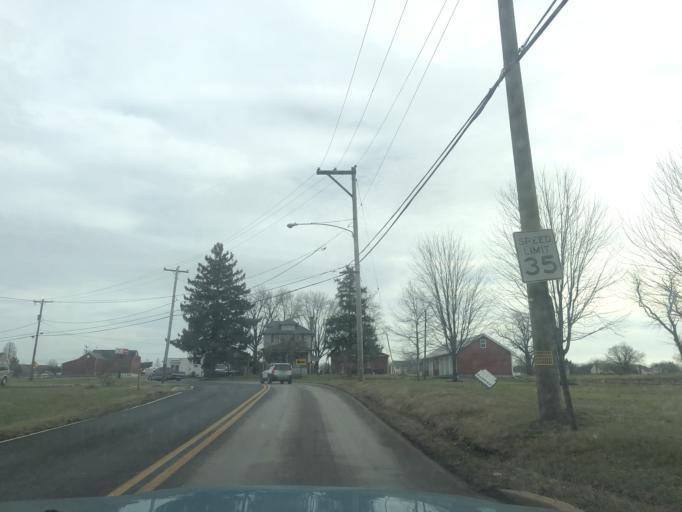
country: US
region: Pennsylvania
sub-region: Montgomery County
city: Harleysville
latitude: 40.2772
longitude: -75.4004
